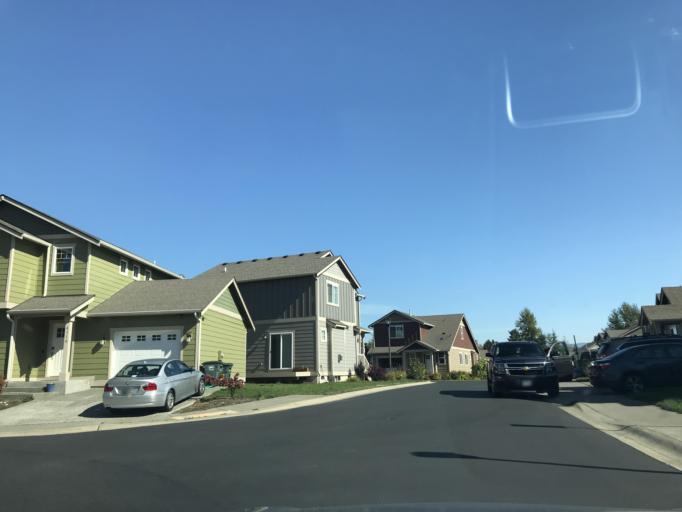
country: US
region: Washington
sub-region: Whatcom County
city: Bellingham
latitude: 48.7973
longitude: -122.5047
